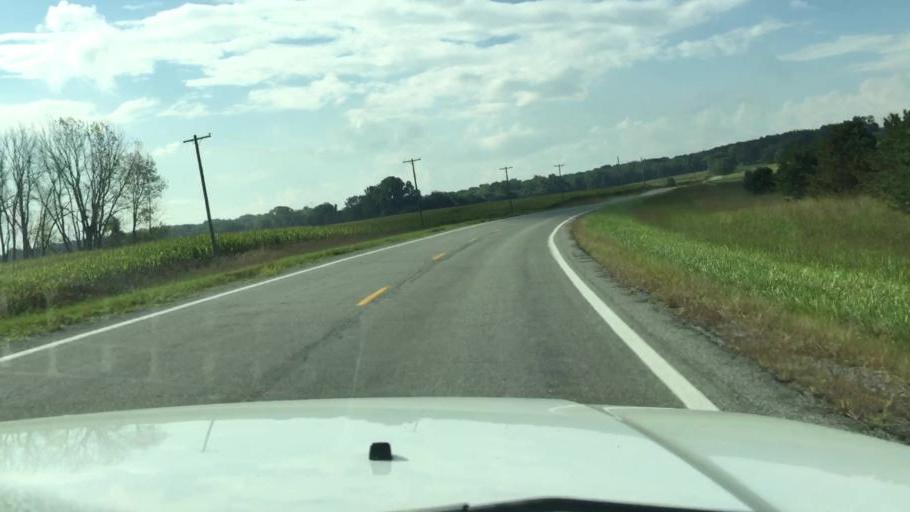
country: US
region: Ohio
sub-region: Champaign County
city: Mechanicsburg
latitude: 40.0497
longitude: -83.6078
